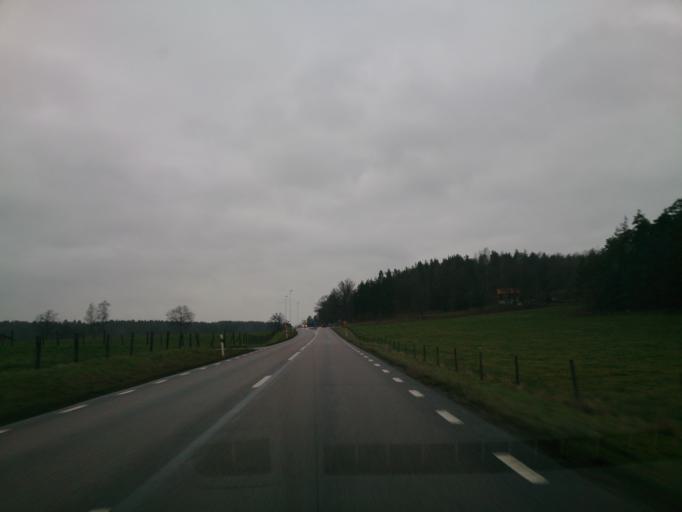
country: SE
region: OEstergoetland
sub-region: Atvidabergs Kommun
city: Atvidaberg
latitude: 58.2903
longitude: 15.8956
